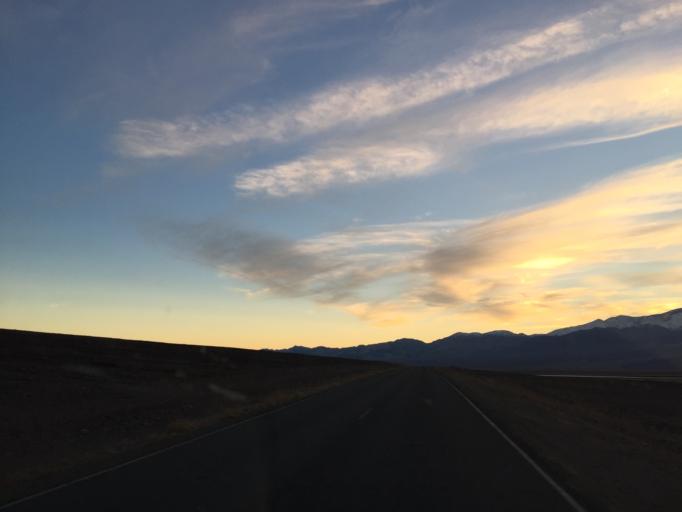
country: US
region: Nevada
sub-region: Nye County
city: Beatty
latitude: 36.1985
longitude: -116.7697
